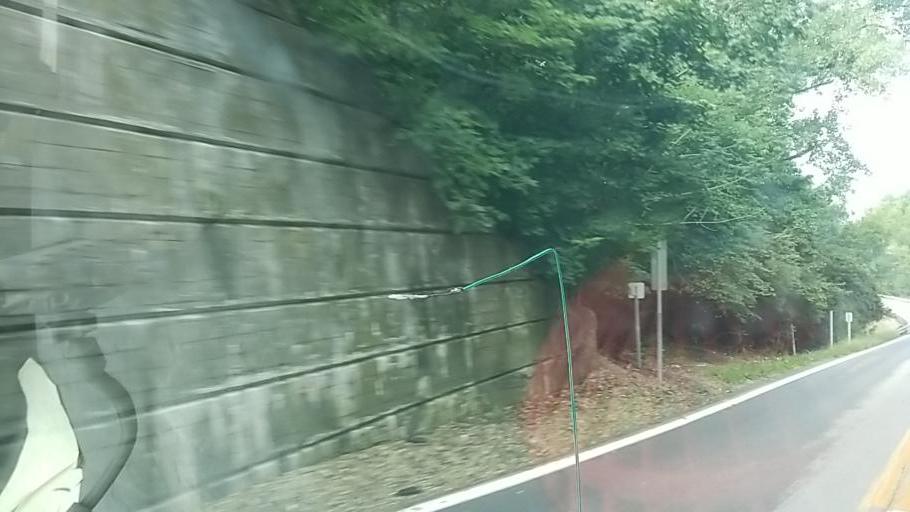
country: US
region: Ohio
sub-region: Franklin County
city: Grove City
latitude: 39.8039
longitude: -83.1576
